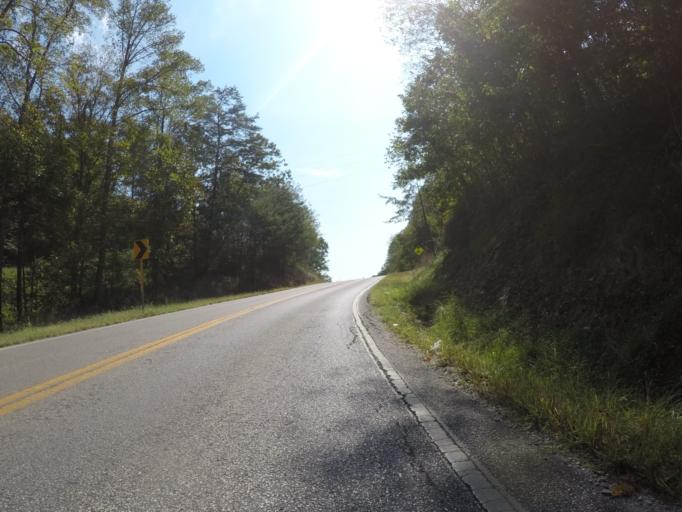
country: US
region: West Virginia
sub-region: Cabell County
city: Lesage
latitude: 38.5289
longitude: -82.3928
